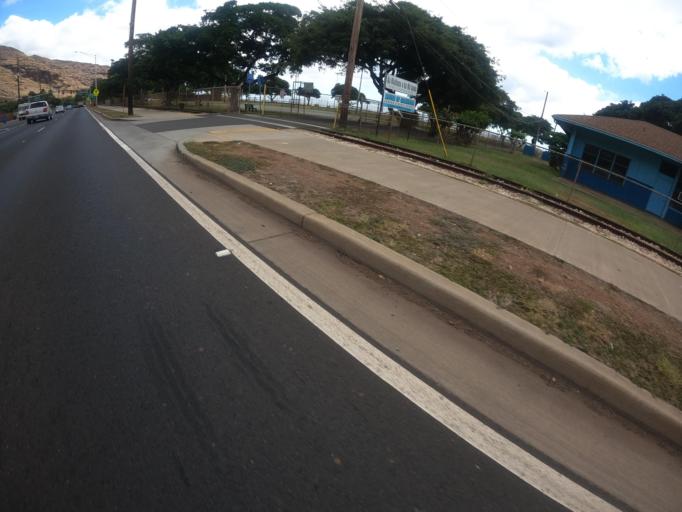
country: US
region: Hawaii
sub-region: Honolulu County
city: Nanakuli
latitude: 21.3795
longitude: -158.1434
